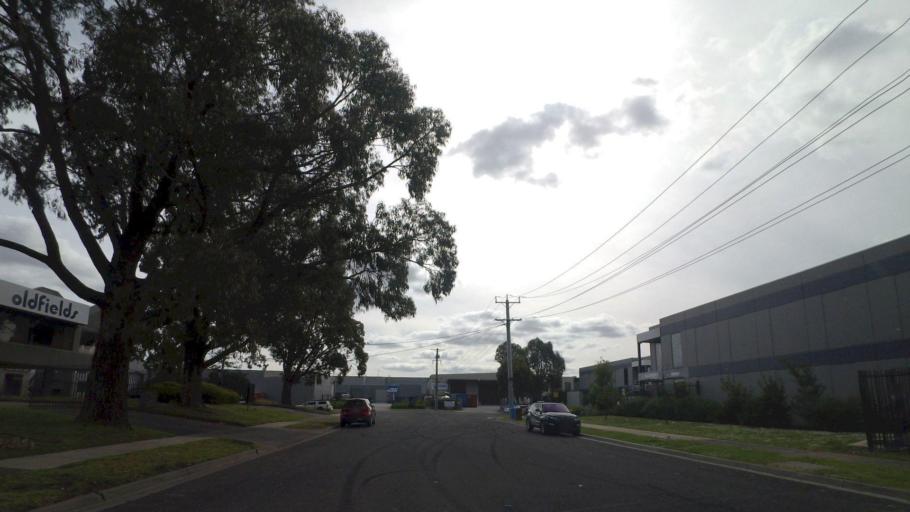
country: AU
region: Victoria
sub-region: Knox
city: Knoxfield
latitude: -37.8998
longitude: 145.2523
